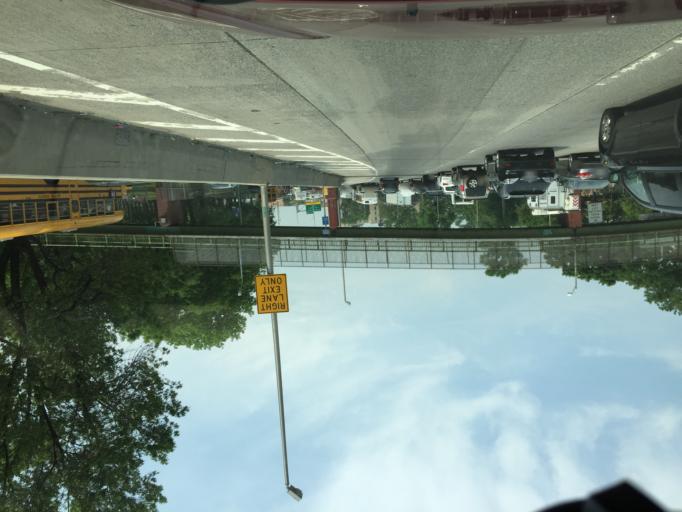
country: US
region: New York
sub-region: Bronx
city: The Bronx
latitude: 40.8484
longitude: -73.8269
